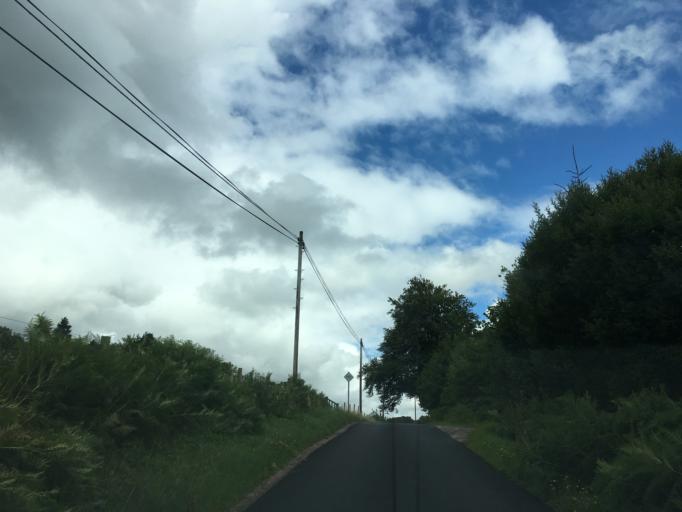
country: GB
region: Scotland
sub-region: Argyll and Bute
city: Oban
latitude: 56.3463
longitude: -5.1895
